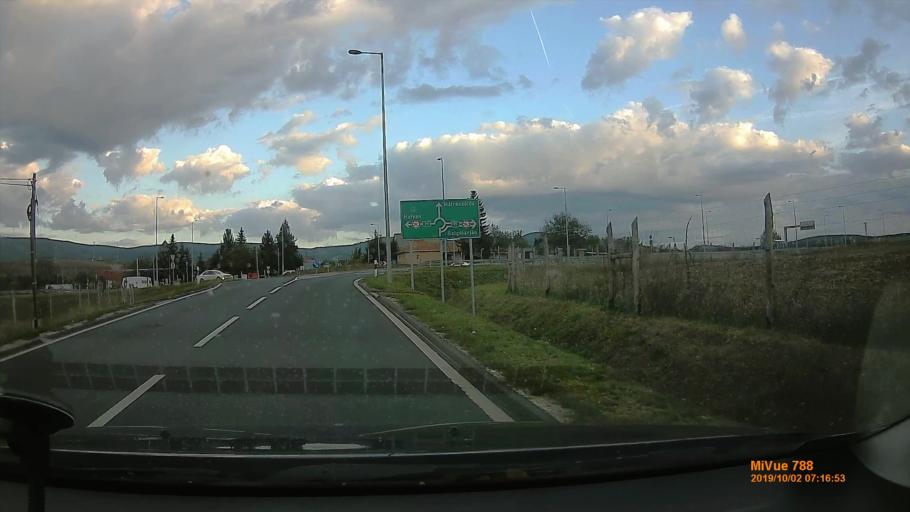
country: HU
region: Nograd
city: Paszto
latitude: 47.9439
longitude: 19.7028
